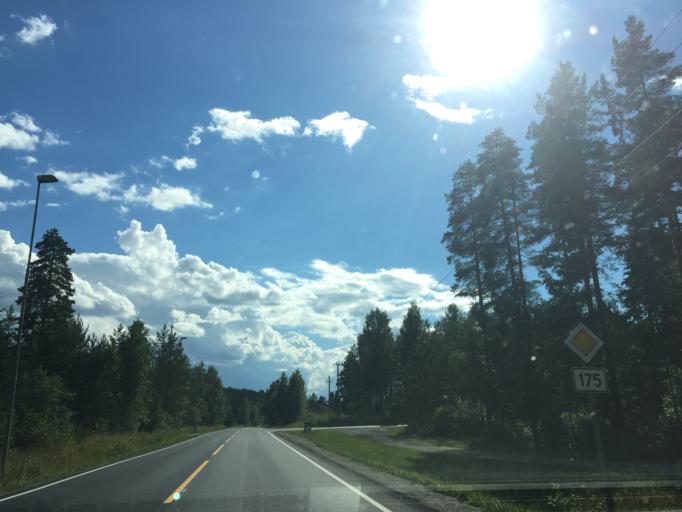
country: NO
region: Hedmark
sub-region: Sor-Odal
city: Skarnes
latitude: 60.1784
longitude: 11.5876
